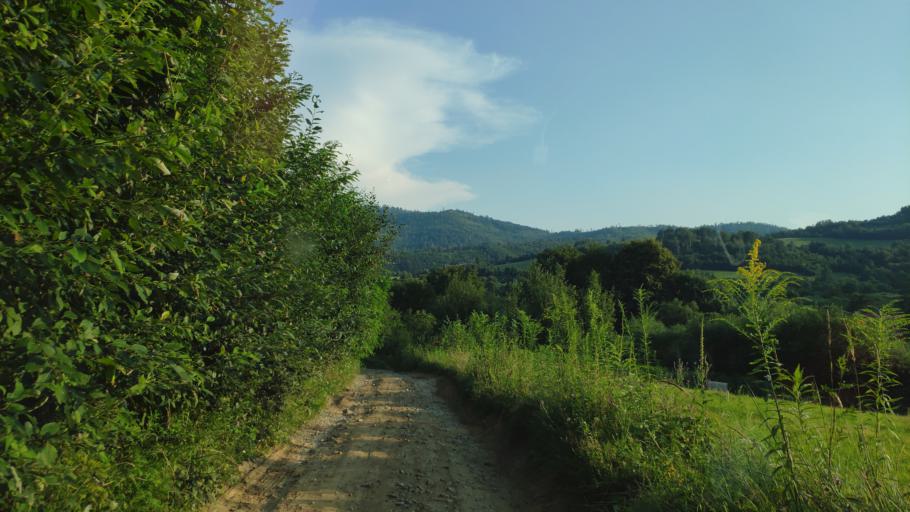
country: SK
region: Kosicky
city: Dobsina
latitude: 48.7160
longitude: 20.2809
